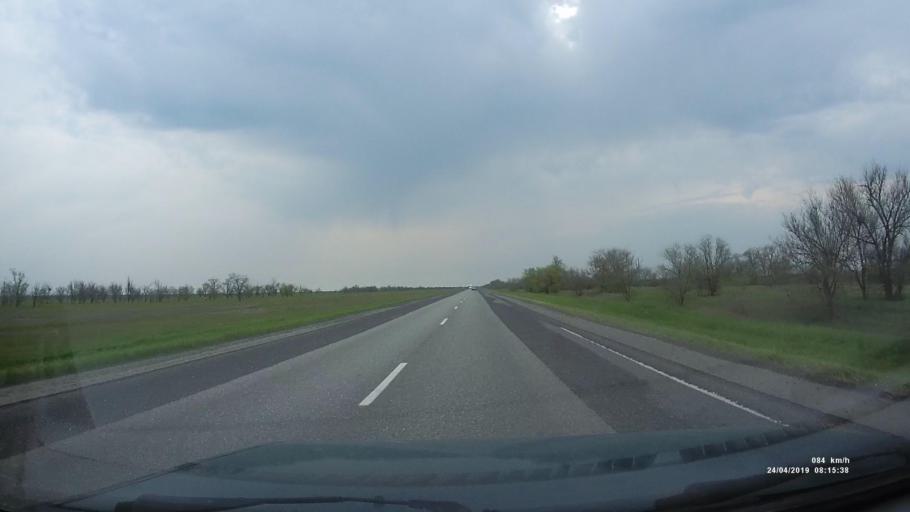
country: RU
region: Kalmykiya
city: Priyutnoye
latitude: 46.0998
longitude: 43.5979
